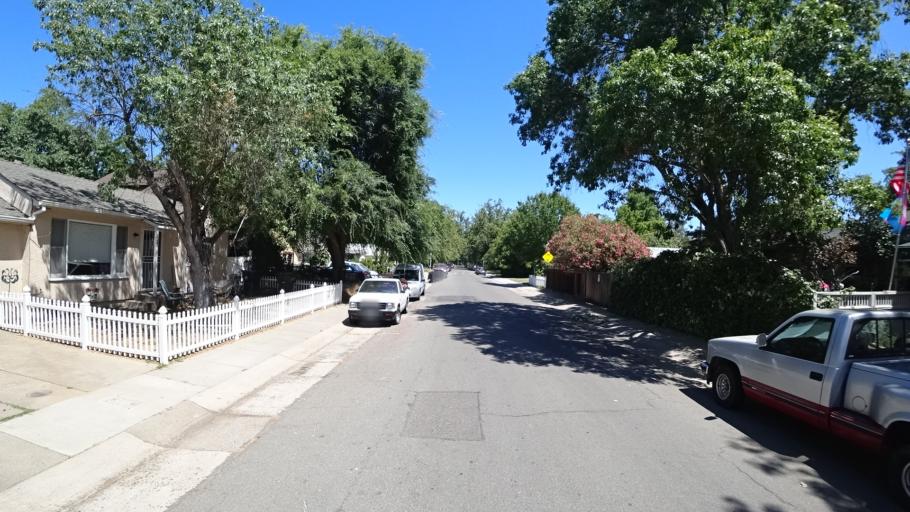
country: US
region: California
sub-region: Sacramento County
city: Sacramento
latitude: 38.5380
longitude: -121.4799
